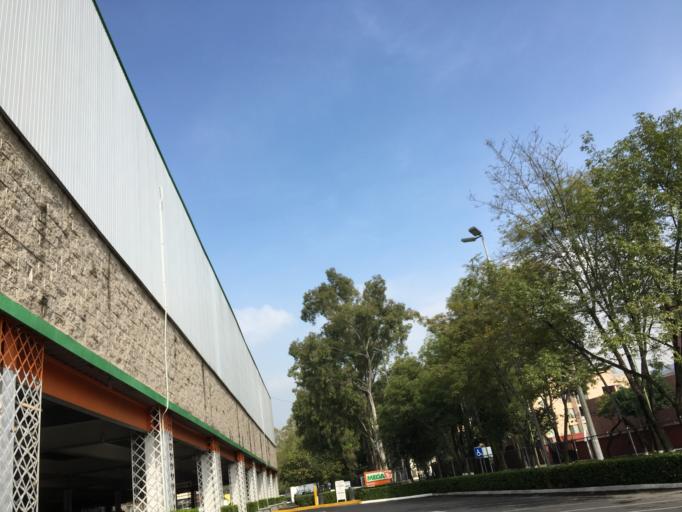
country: MX
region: Mexico City
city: Tlalpan
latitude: 19.2861
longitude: -99.1376
